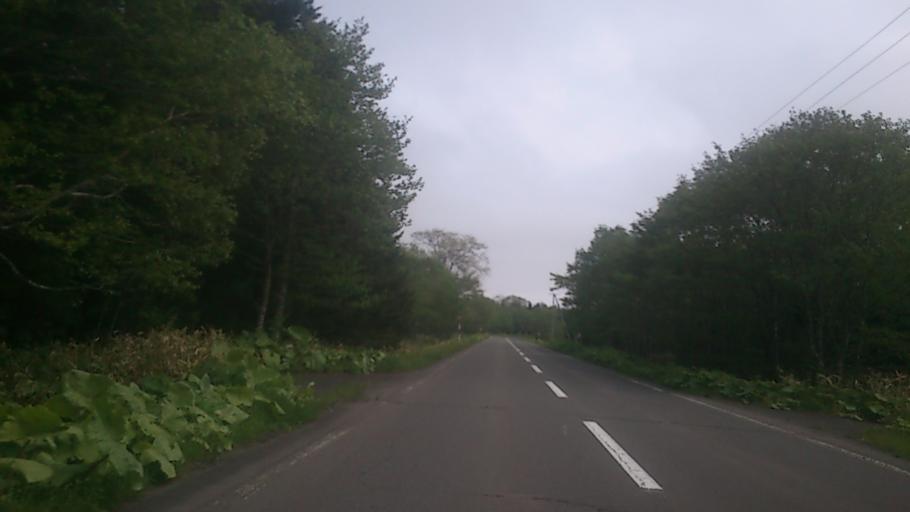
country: JP
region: Hokkaido
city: Nemuro
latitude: 43.1927
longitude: 145.3246
